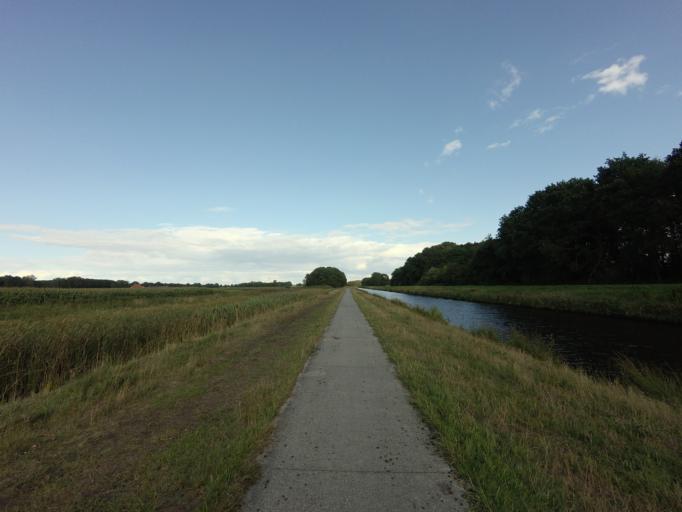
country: NL
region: Friesland
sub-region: Gemeente Heerenveen
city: Jubbega
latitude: 52.9948
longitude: 6.2184
